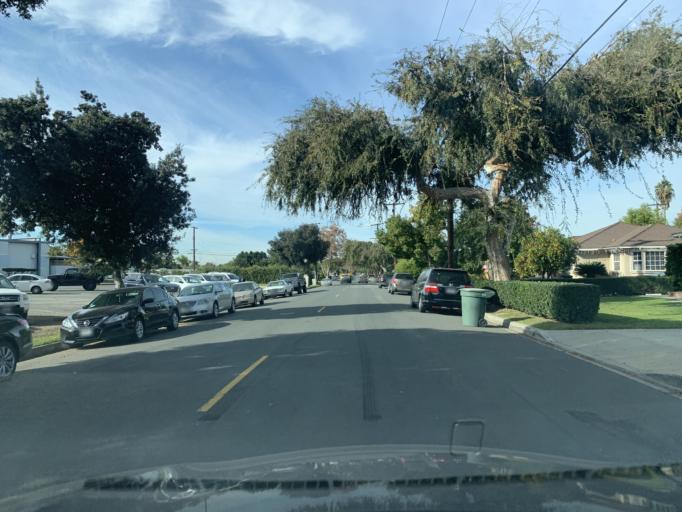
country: US
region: California
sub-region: Los Angeles County
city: West Covina
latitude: 34.0755
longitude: -117.9273
